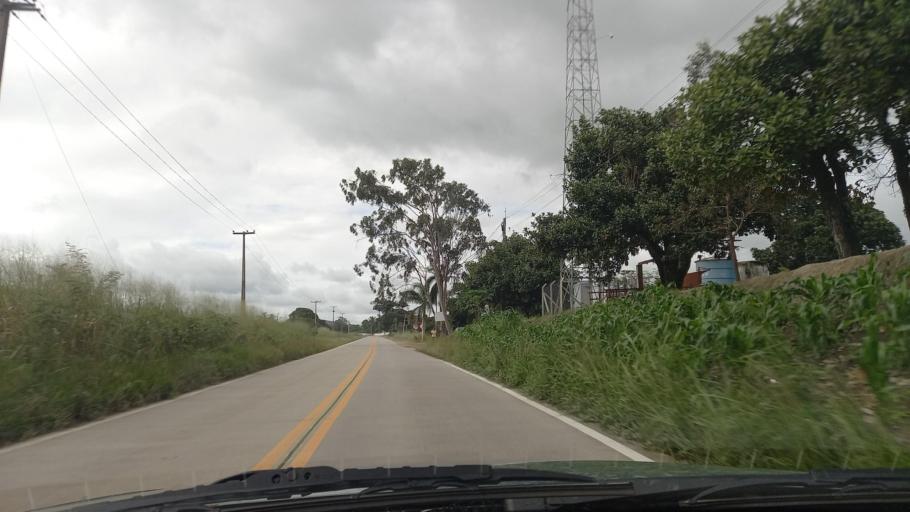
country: BR
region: Pernambuco
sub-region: Quipapa
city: Quipapa
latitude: -8.7960
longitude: -35.9948
